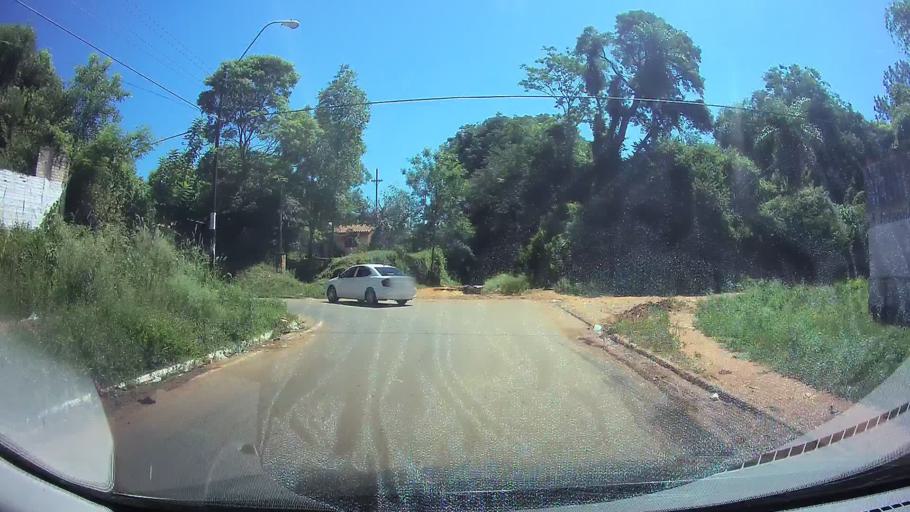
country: PY
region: Central
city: Aregua
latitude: -25.3172
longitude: -57.3906
